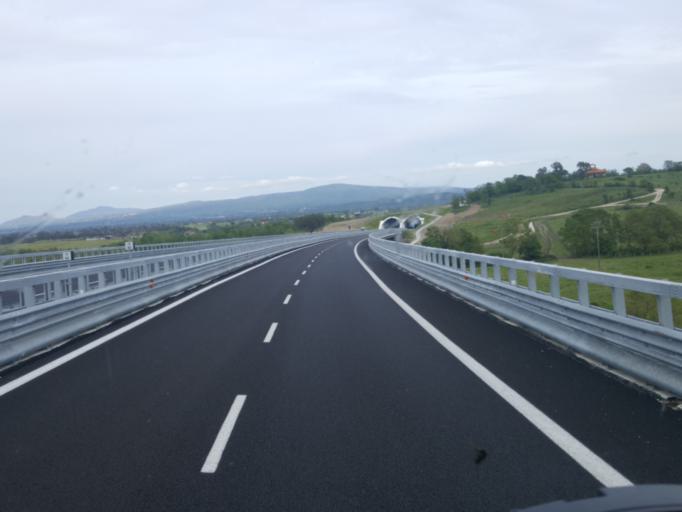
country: IT
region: Latium
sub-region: Provincia di Viterbo
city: Monte Romano
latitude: 42.2966
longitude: 11.9505
